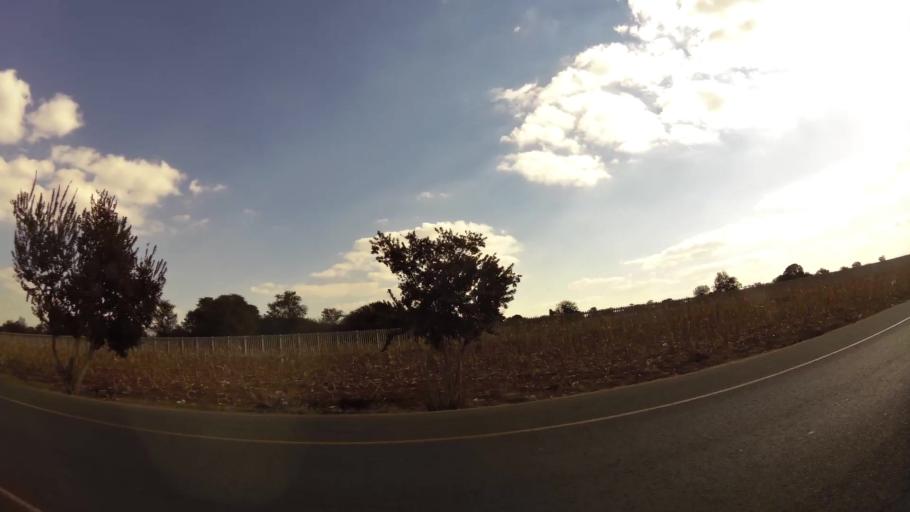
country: ZA
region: Gauteng
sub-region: Ekurhuleni Metropolitan Municipality
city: Tembisa
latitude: -25.9616
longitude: 28.1959
